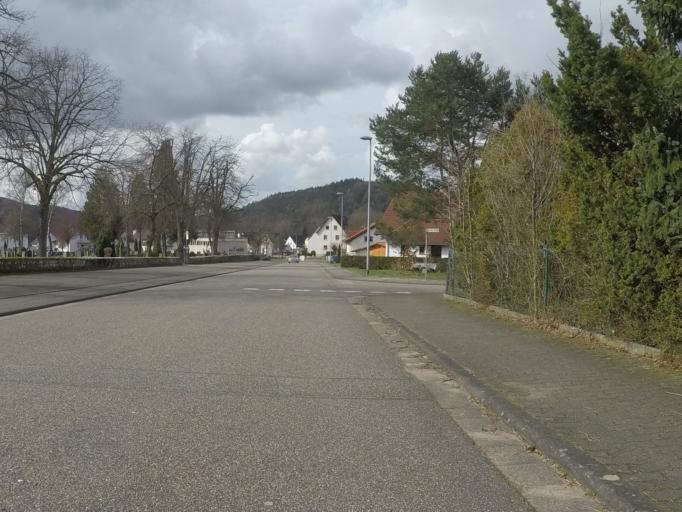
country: DE
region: Rheinland-Pfalz
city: Munchweiler an der Rodalbe
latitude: 49.2172
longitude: 7.7091
